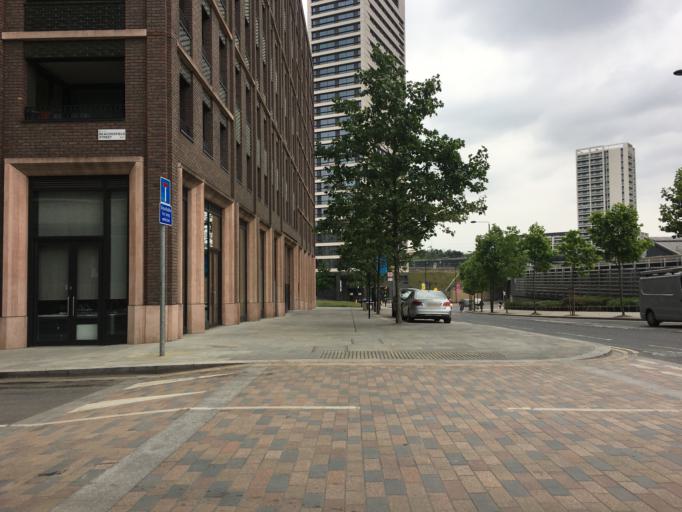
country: GB
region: England
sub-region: Greater London
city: Barnsbury
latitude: 51.5387
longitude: -0.1236
